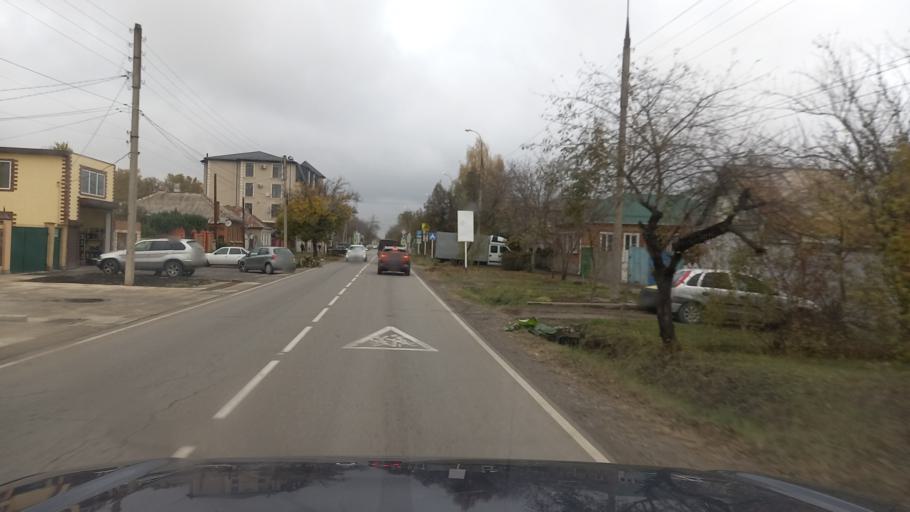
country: RU
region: Adygeya
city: Maykop
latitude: 44.6065
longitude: 40.0716
